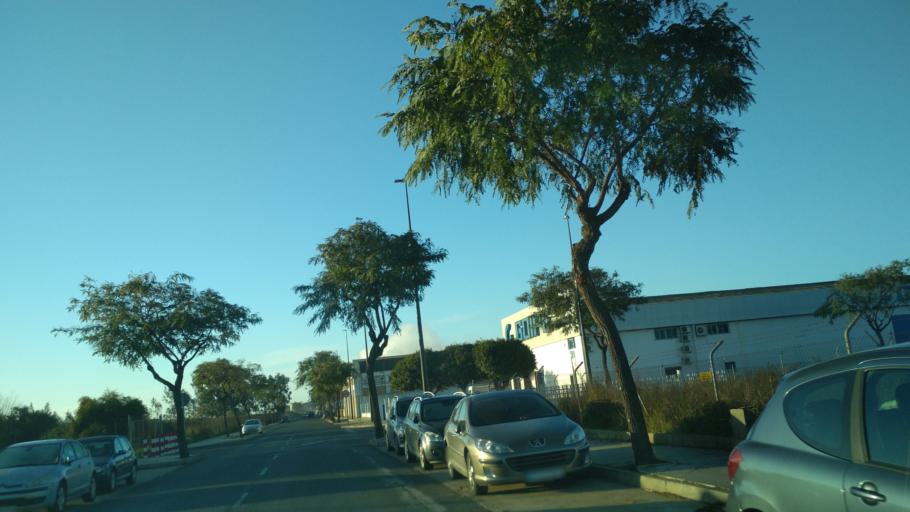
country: ES
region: Andalusia
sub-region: Provincia de Huelva
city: Huelva
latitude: 37.2402
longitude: -6.9473
